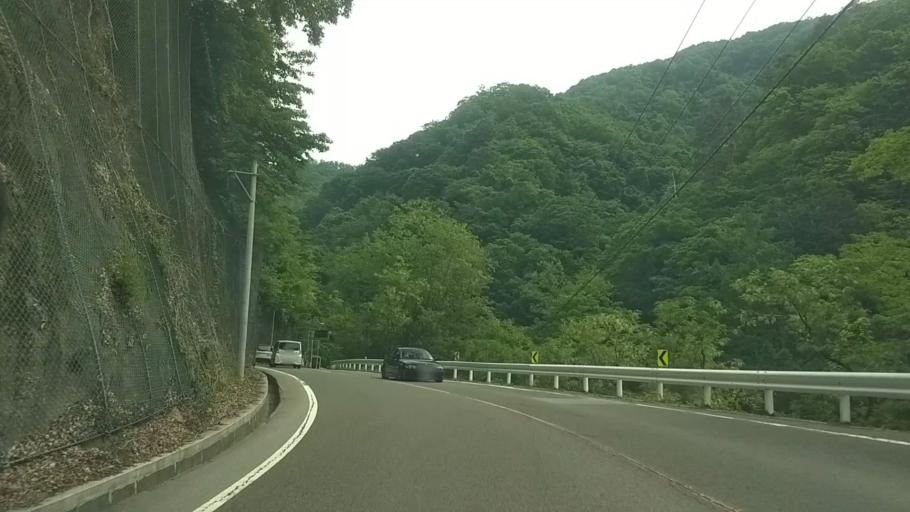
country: JP
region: Yamanashi
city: Isawa
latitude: 35.5582
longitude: 138.5901
